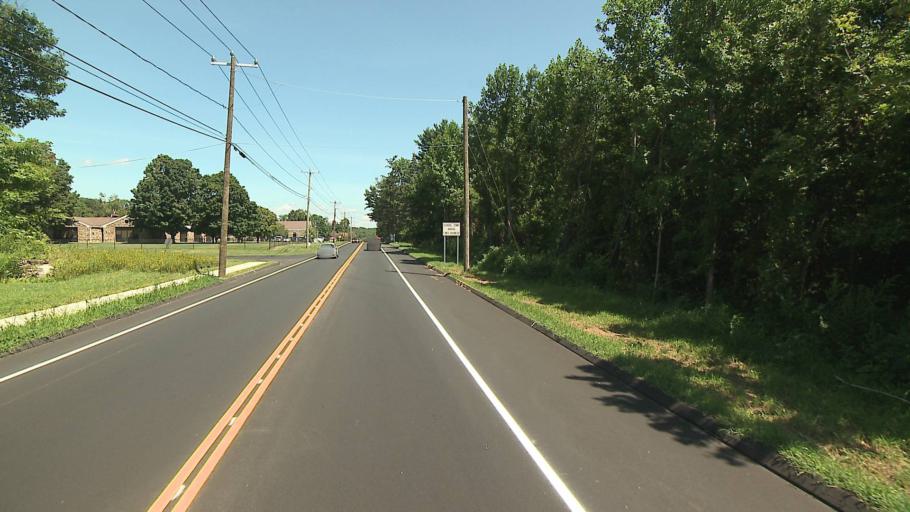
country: US
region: Connecticut
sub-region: Fairfield County
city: Trumbull
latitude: 41.3075
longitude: -73.2223
